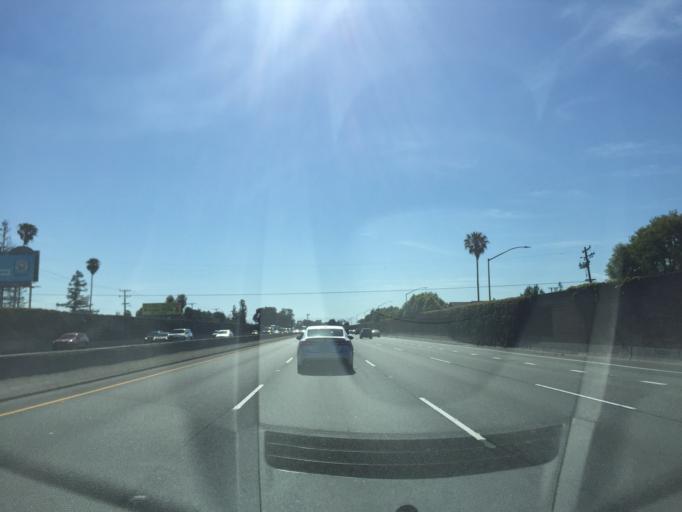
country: US
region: California
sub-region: San Mateo County
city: North Fair Oaks
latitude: 37.4860
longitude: -122.1941
